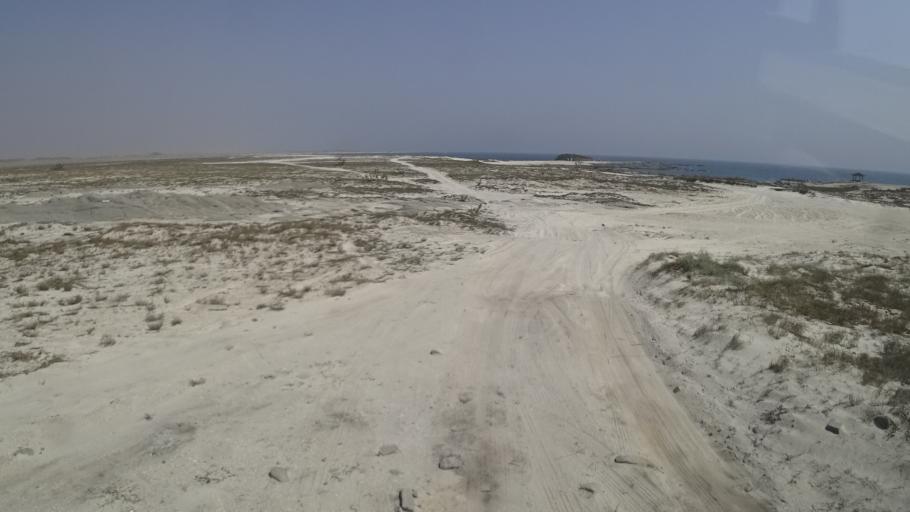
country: OM
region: Zufar
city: Salalah
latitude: 16.9706
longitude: 54.7030
